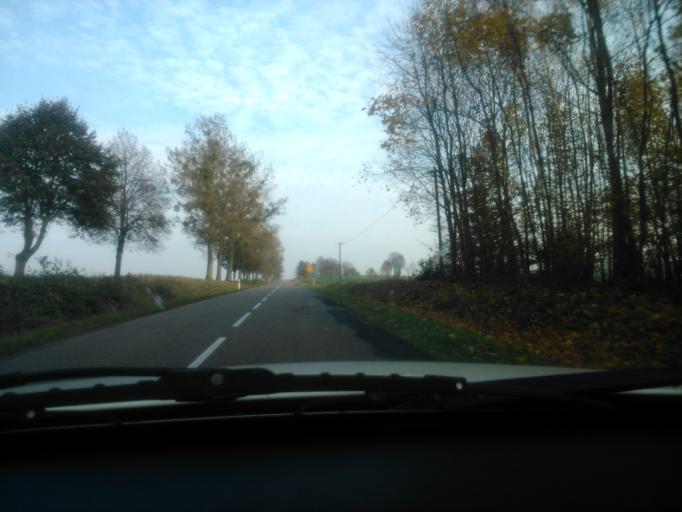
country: PL
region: Warmian-Masurian Voivodeship
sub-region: Powiat dzialdowski
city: Lidzbark
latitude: 53.2601
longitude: 19.7549
